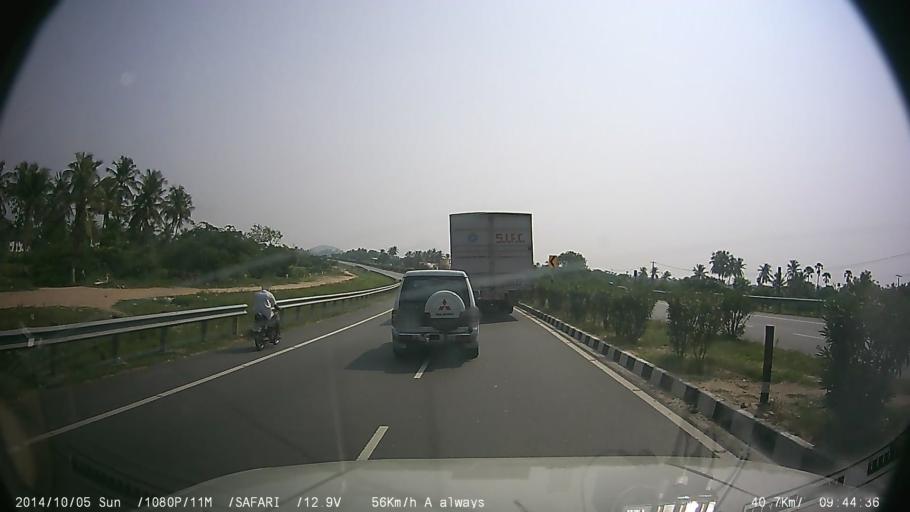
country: IN
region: Tamil Nadu
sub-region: Erode
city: Bhavani
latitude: 11.4497
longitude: 77.7750
